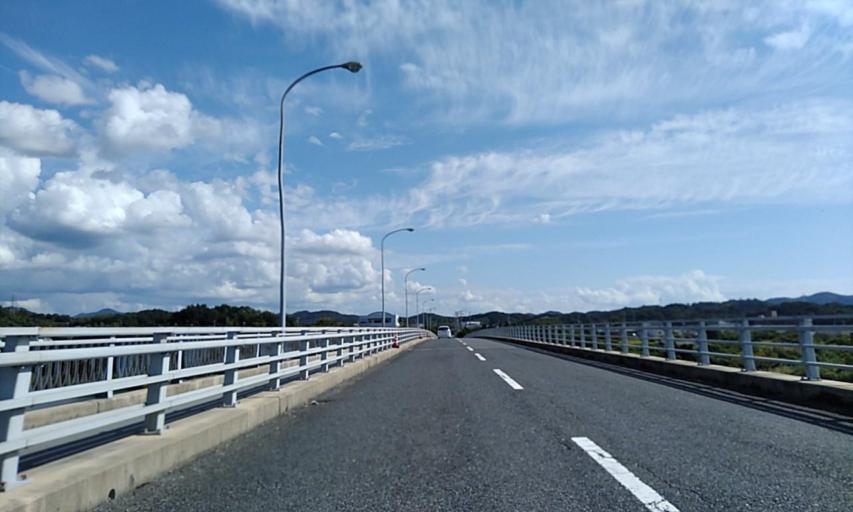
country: JP
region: Wakayama
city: Gobo
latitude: 33.8913
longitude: 135.1670
